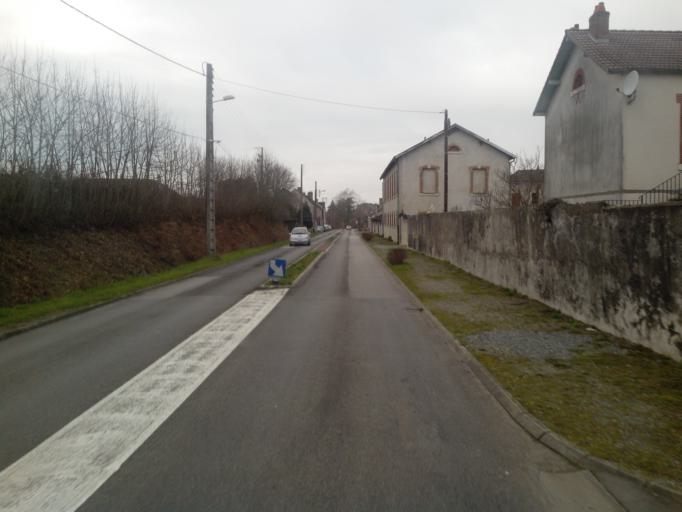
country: FR
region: Limousin
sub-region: Departement de la Haute-Vienne
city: Magnac-Laval
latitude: 46.2119
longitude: 1.1744
